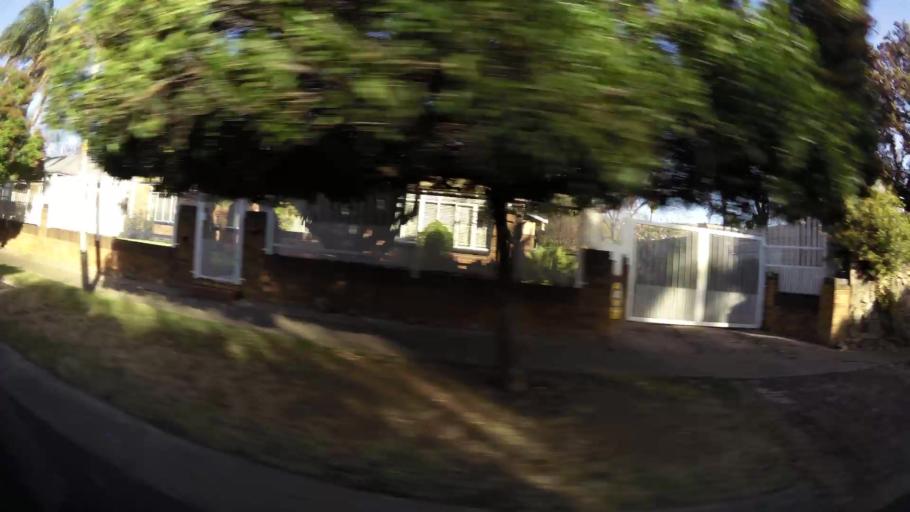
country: ZA
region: Gauteng
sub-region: City of Tshwane Metropolitan Municipality
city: Pretoria
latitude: -25.7239
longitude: 28.2115
